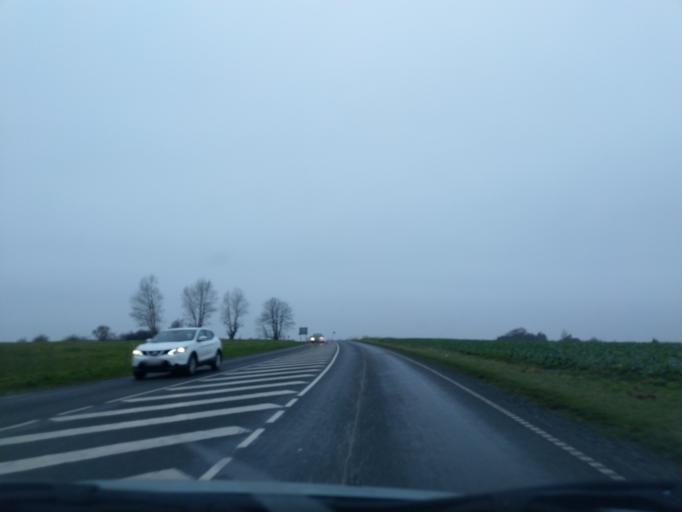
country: DK
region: Zealand
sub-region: Vordingborg Kommune
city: Praesto
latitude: 55.1186
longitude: 12.0209
